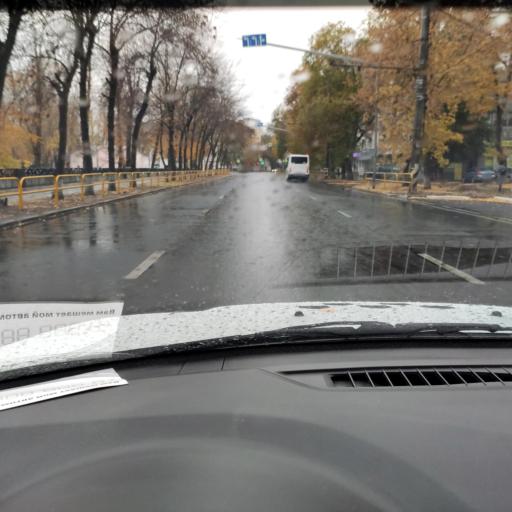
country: RU
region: Samara
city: Tol'yatti
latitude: 53.5098
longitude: 49.4223
